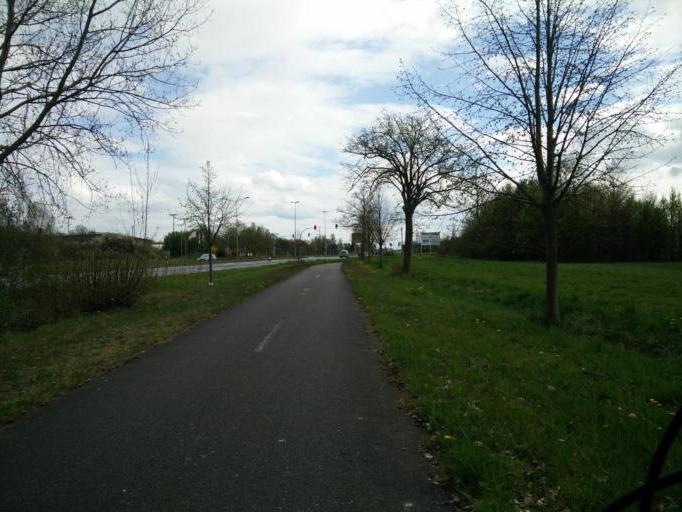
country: DE
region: Mecklenburg-Vorpommern
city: Nienhagen
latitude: 54.1296
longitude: 12.1655
